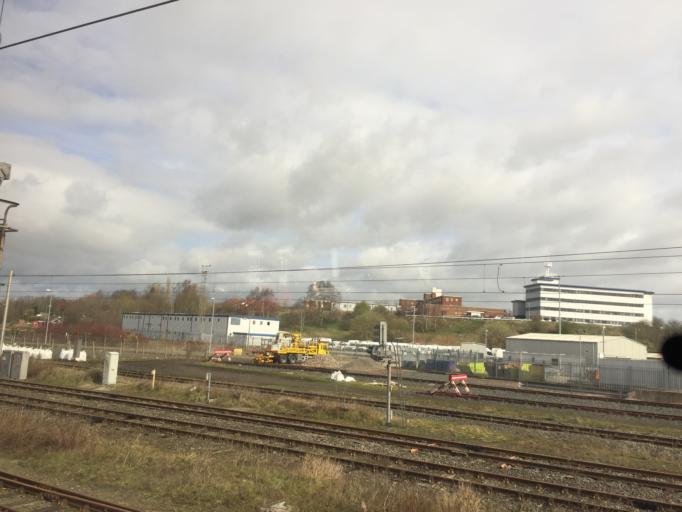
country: GB
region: England
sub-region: Cumbria
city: Carlisle
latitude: 54.8818
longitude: -2.9218
